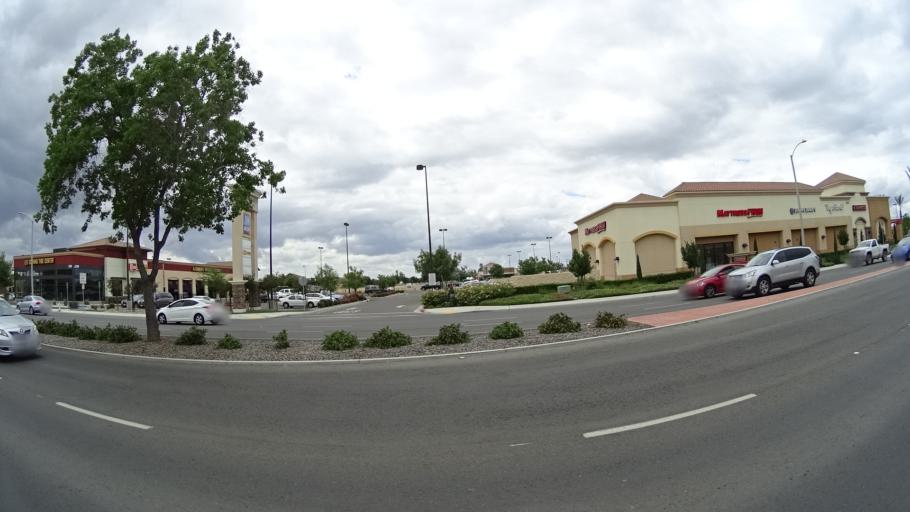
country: US
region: California
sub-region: Kings County
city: Hanford
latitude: 36.3270
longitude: -119.6728
